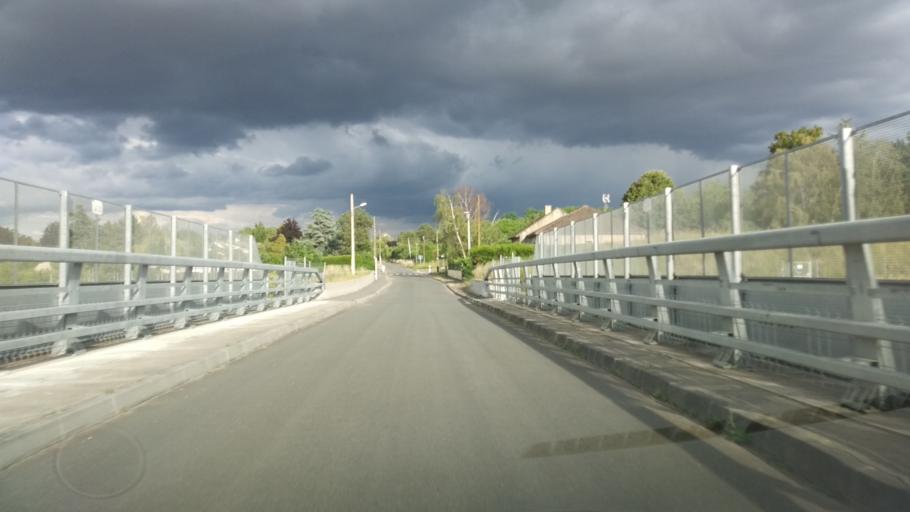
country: FR
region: Poitou-Charentes
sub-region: Departement de la Vienne
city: Migne-Auxances
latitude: 46.6264
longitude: 0.3410
